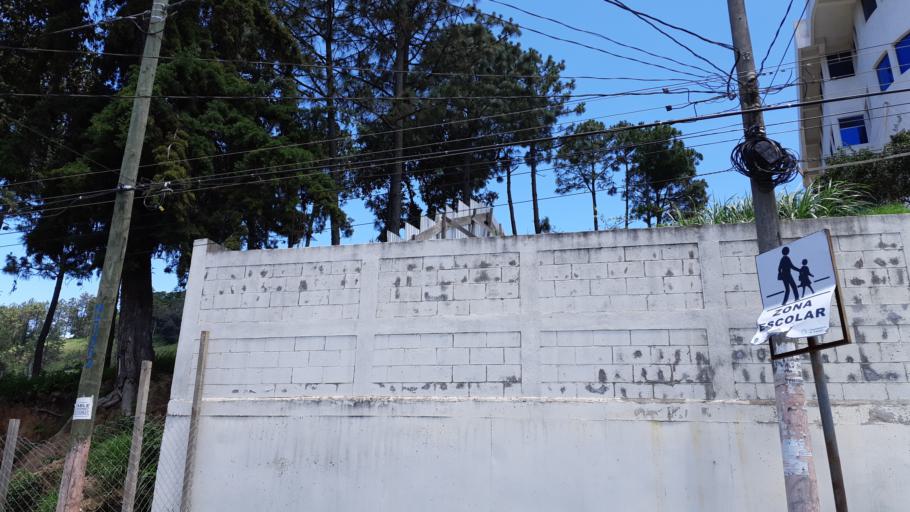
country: GT
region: Chimaltenango
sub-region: Municipio de Chimaltenango
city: Chimaltenango
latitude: 14.6662
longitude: -90.8498
